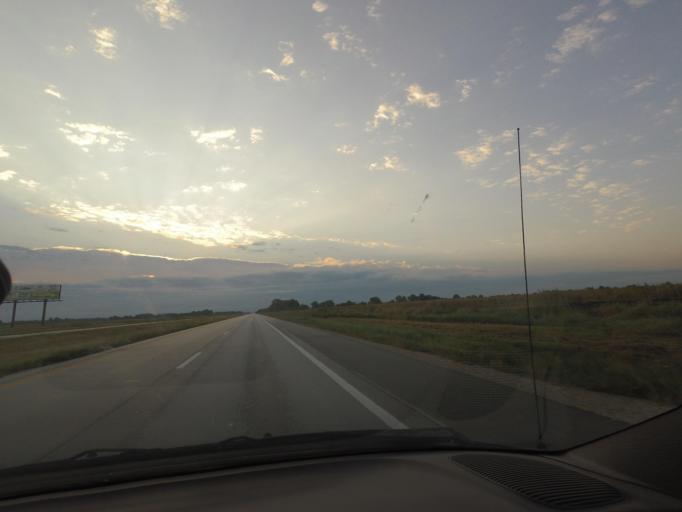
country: US
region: Missouri
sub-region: Shelby County
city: Shelbina
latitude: 39.7370
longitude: -92.2259
